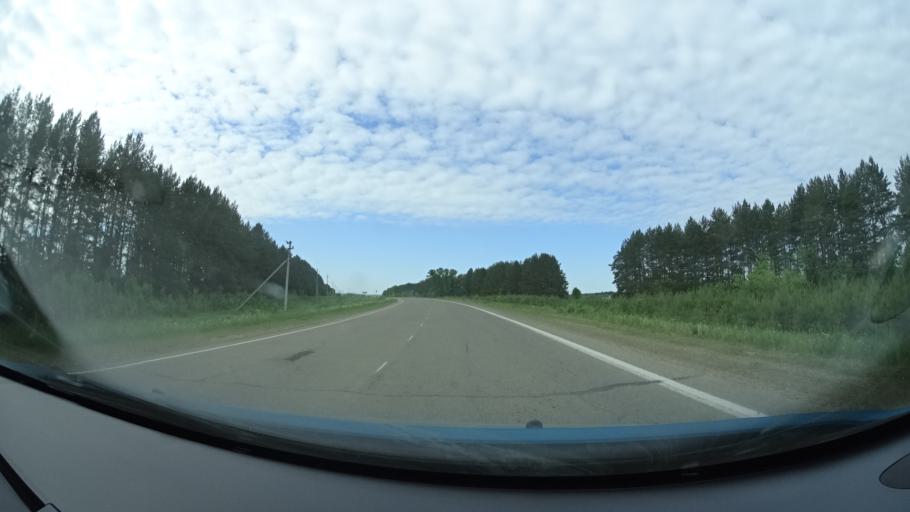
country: RU
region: Perm
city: Kuyeda
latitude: 56.4807
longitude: 55.5919
